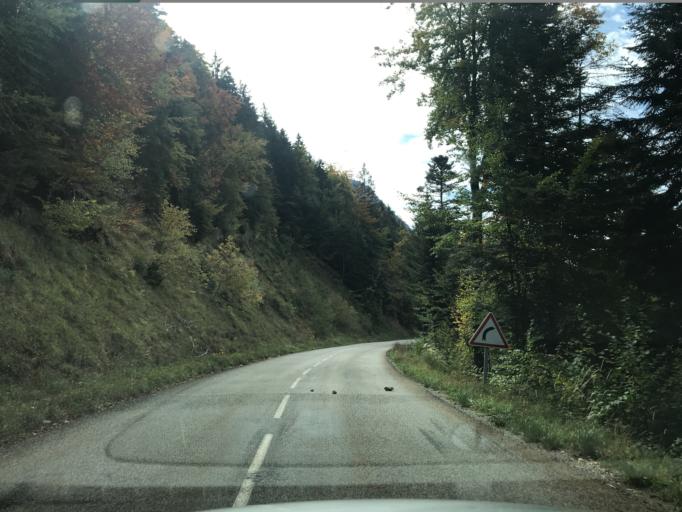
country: FR
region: Rhone-Alpes
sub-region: Departement de la Savoie
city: Les Echelles
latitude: 45.4608
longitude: 5.8207
